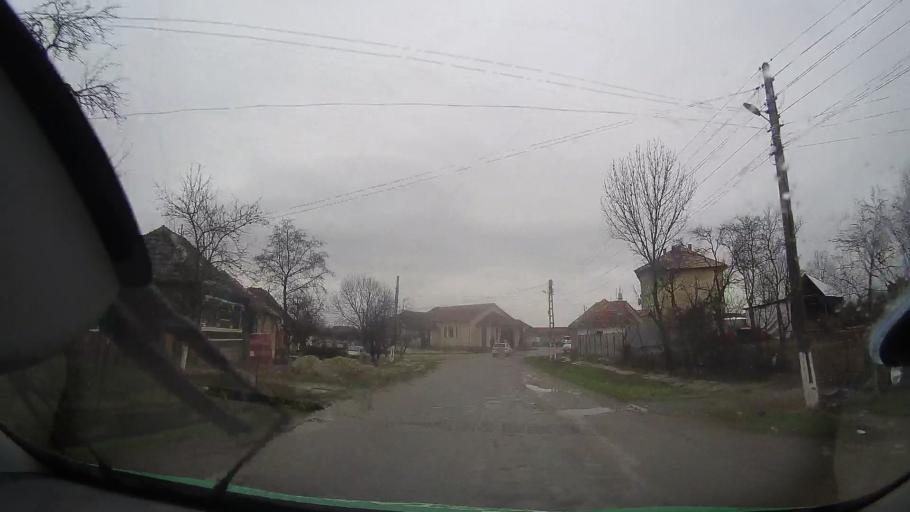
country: RO
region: Bihor
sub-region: Comuna Olcea
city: Olcea
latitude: 46.6830
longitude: 21.9820
